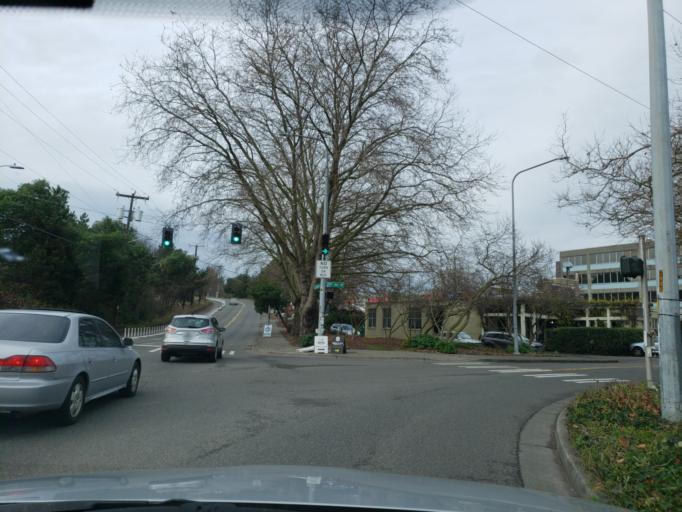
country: US
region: Washington
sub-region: King County
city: Seattle
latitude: 47.6557
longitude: -122.3833
